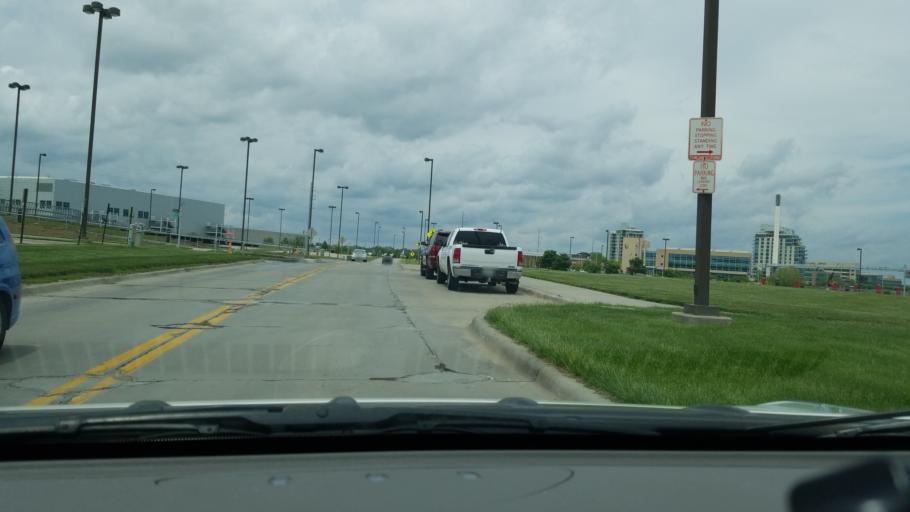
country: US
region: Nebraska
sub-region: Douglas County
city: Omaha
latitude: 41.2611
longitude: -95.9240
